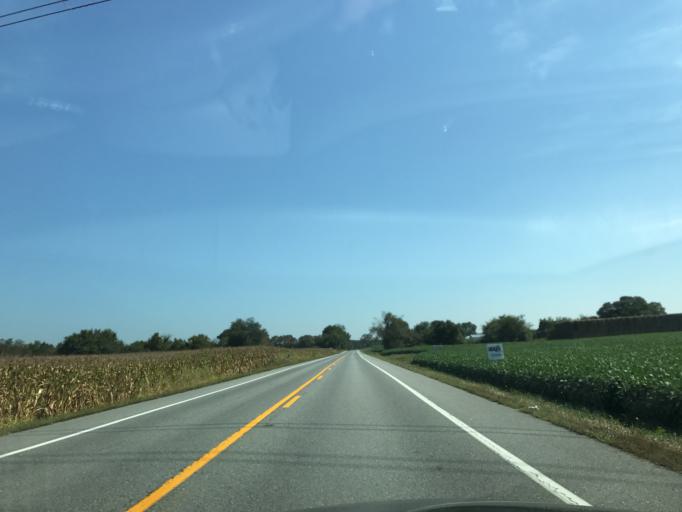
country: US
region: Delaware
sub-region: New Castle County
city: Townsend
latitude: 39.3034
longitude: -75.8063
